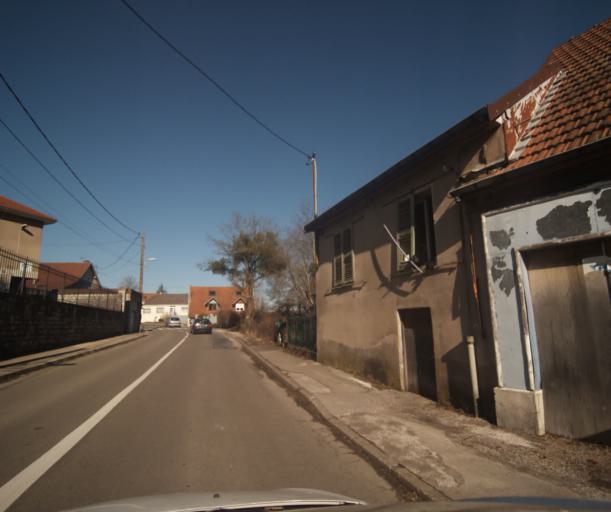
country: FR
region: Franche-Comte
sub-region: Departement du Doubs
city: Thise
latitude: 47.2665
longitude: 6.0499
